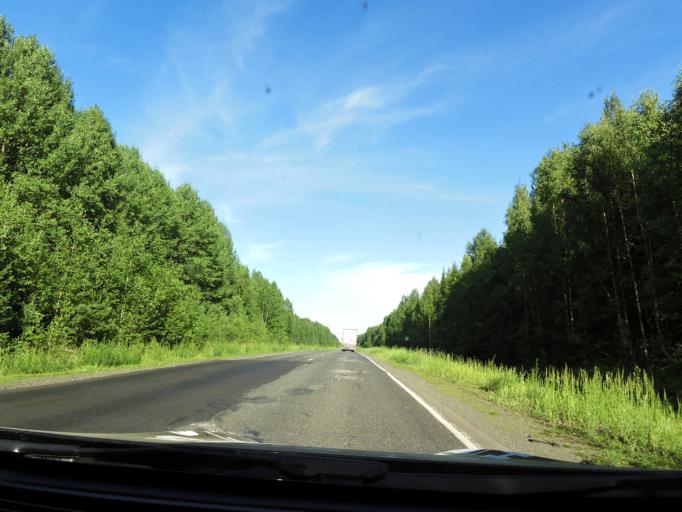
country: RU
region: Kirov
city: Chernaya Kholunitsa
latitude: 58.8830
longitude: 51.4177
